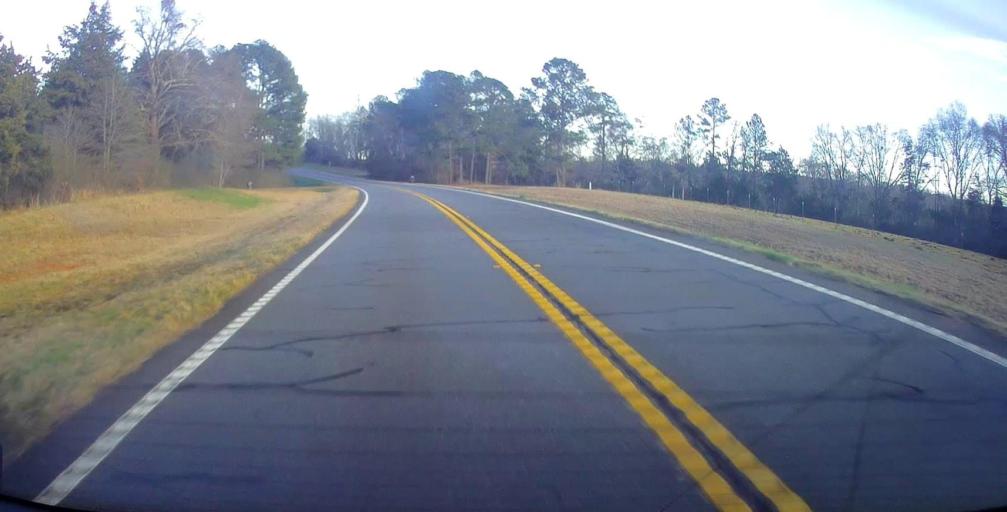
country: US
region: Georgia
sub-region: Talbot County
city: Talbotton
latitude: 32.7847
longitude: -84.5267
